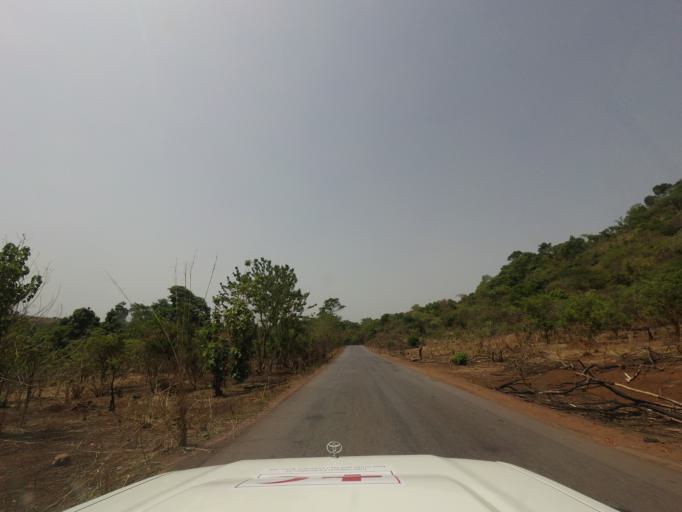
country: GN
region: Mamou
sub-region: Mamou Prefecture
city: Mamou
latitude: 10.2017
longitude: -12.4669
